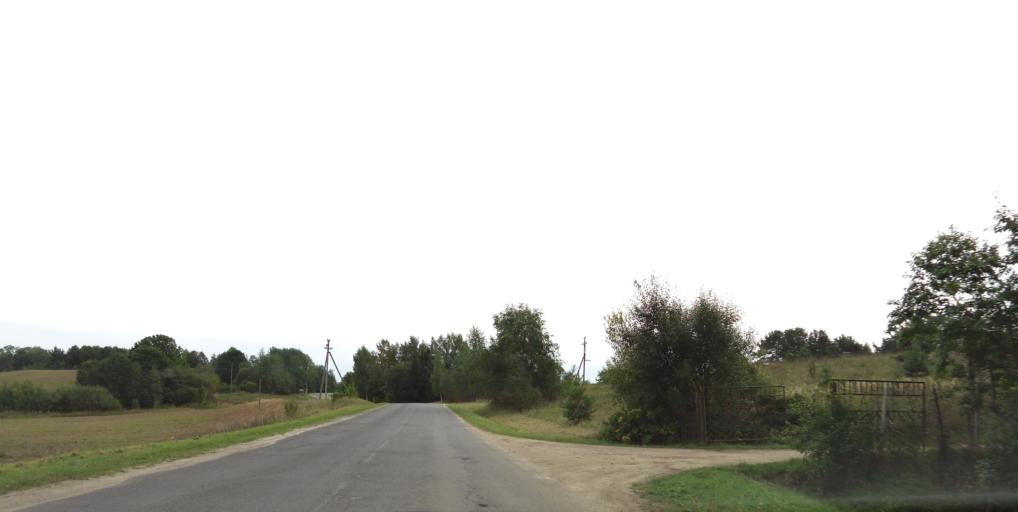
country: LT
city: Grigiskes
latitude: 54.7655
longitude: 25.0351
